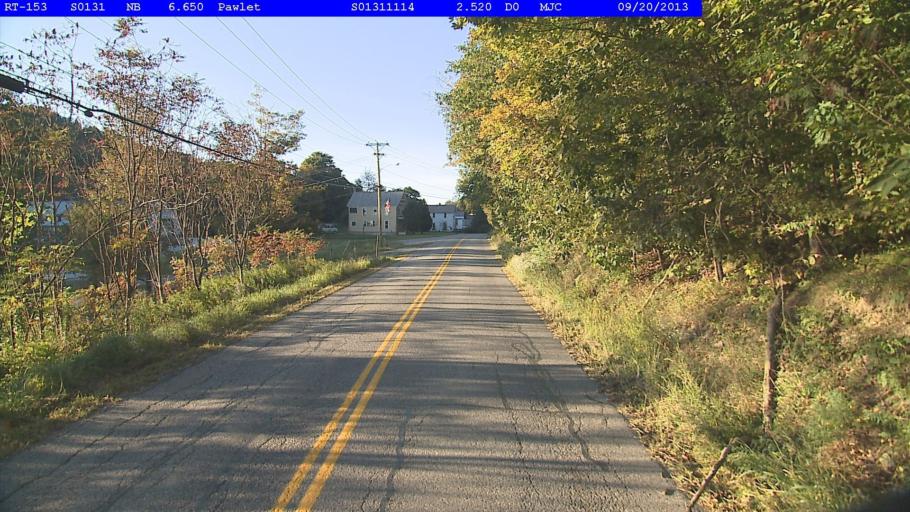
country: US
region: New York
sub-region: Washington County
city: Granville
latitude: 43.3493
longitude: -73.2492
